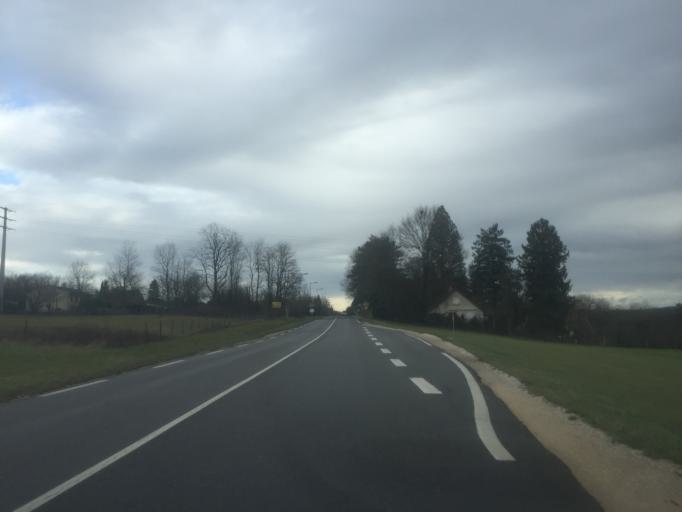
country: FR
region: Franche-Comte
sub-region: Departement du Doubs
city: Saint-Vit
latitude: 47.1750
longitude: 5.7862
